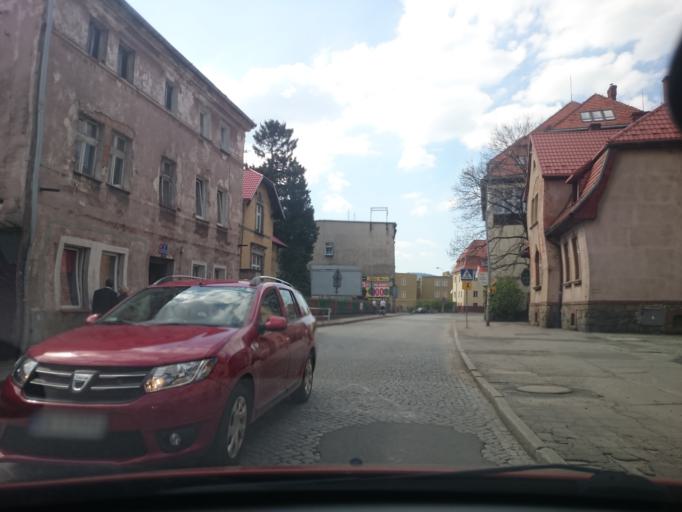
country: PL
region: Lower Silesian Voivodeship
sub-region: Powiat klodzki
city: Bystrzyca Klodzka
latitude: 50.2983
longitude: 16.6488
